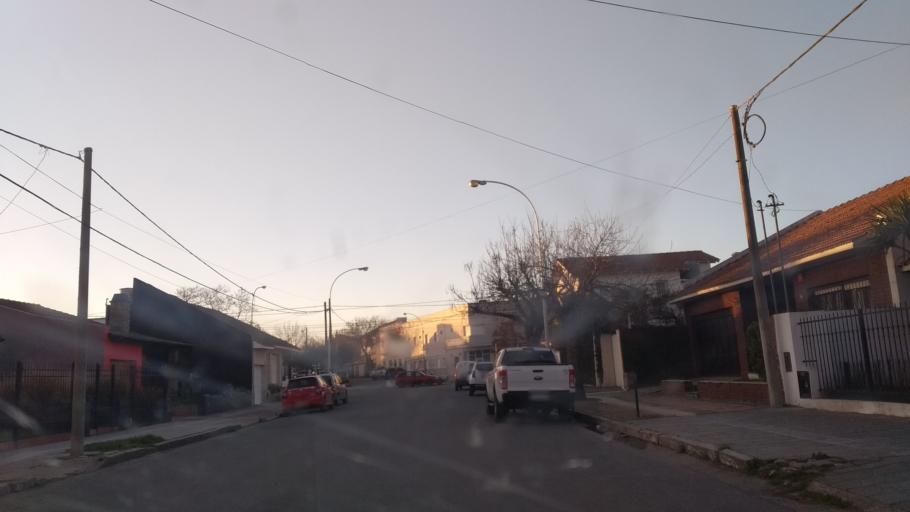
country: AR
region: Buenos Aires
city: Necochea
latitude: -38.5795
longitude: -58.7325
